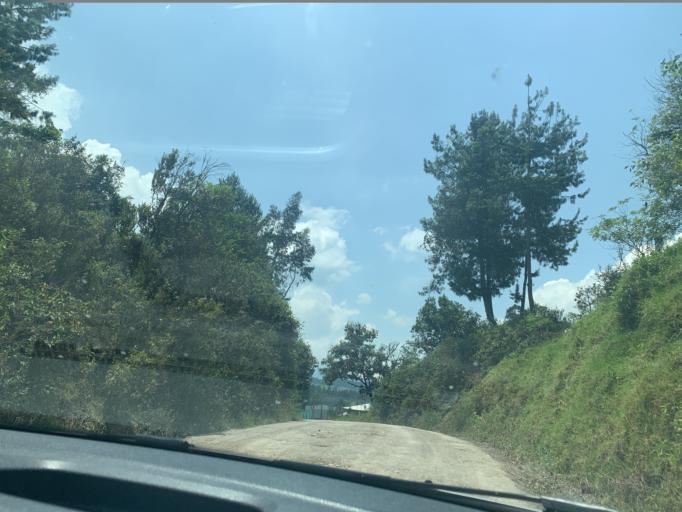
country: CO
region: Boyaca
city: Chiquinquira
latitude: 5.5901
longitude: -73.7539
